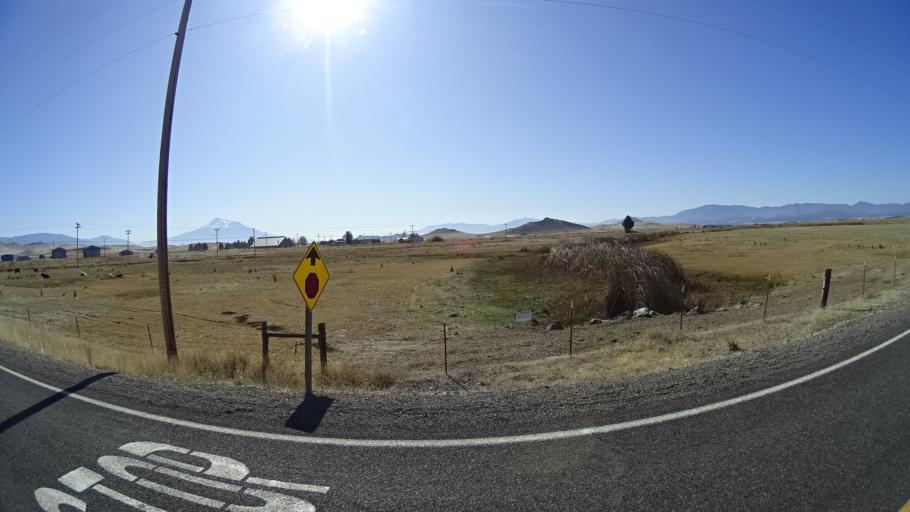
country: US
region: California
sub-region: Siskiyou County
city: Montague
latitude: 41.7707
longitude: -122.4832
